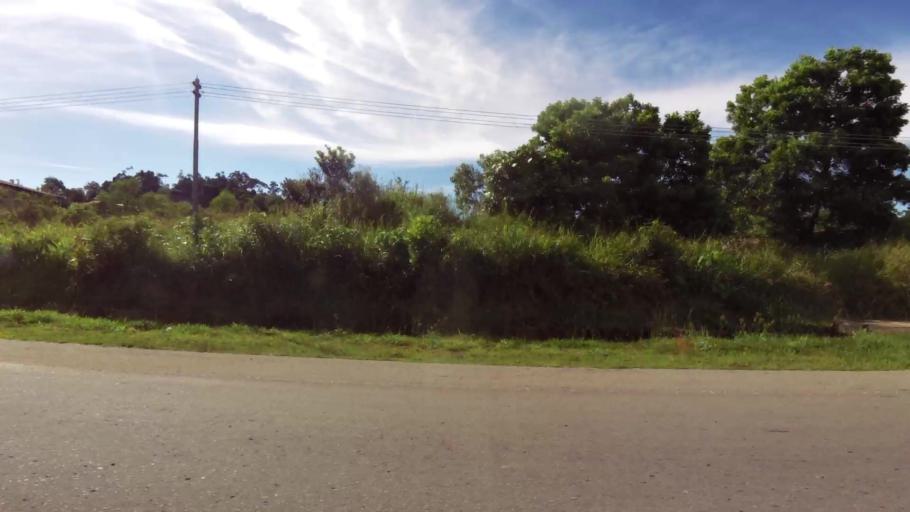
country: BN
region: Brunei and Muara
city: Bandar Seri Begawan
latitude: 5.0124
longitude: 115.0330
